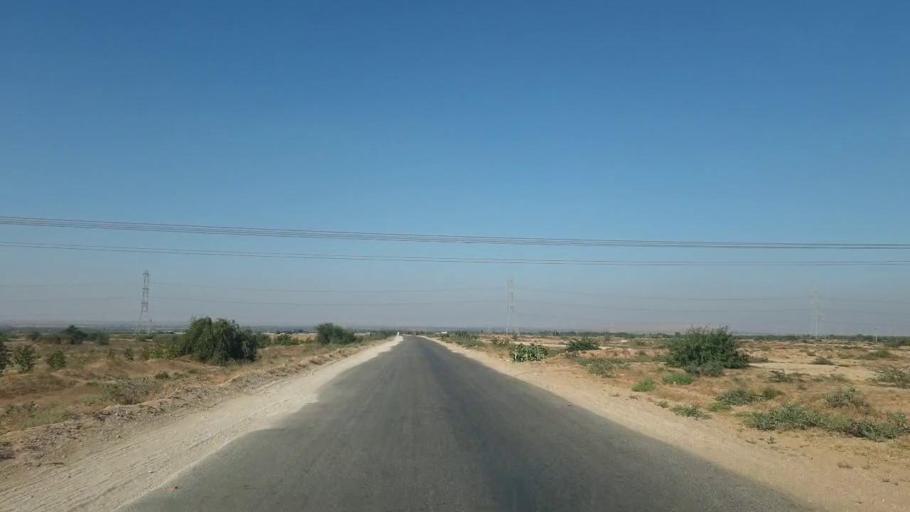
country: PK
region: Sindh
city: Gharo
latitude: 25.1749
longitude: 67.6598
